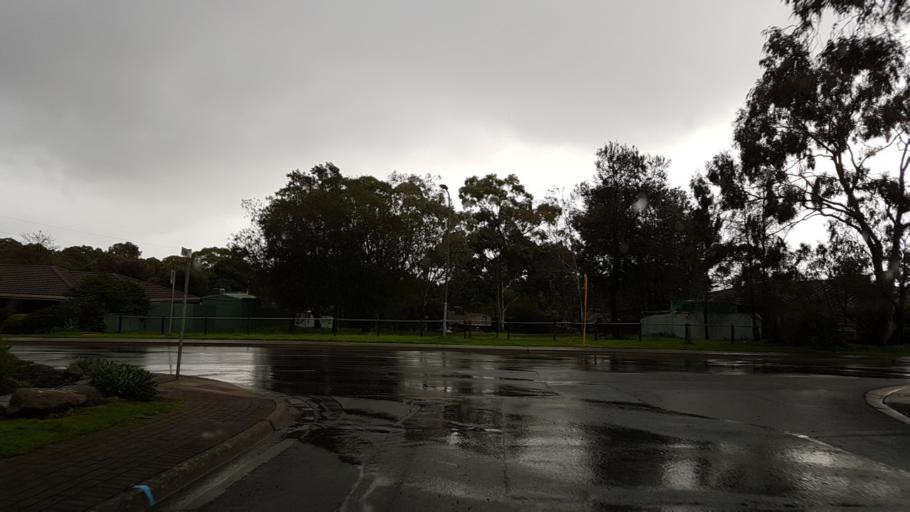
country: AU
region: South Australia
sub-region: Onkaparinga
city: Craigburn Farm
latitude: -35.0849
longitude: 138.5875
